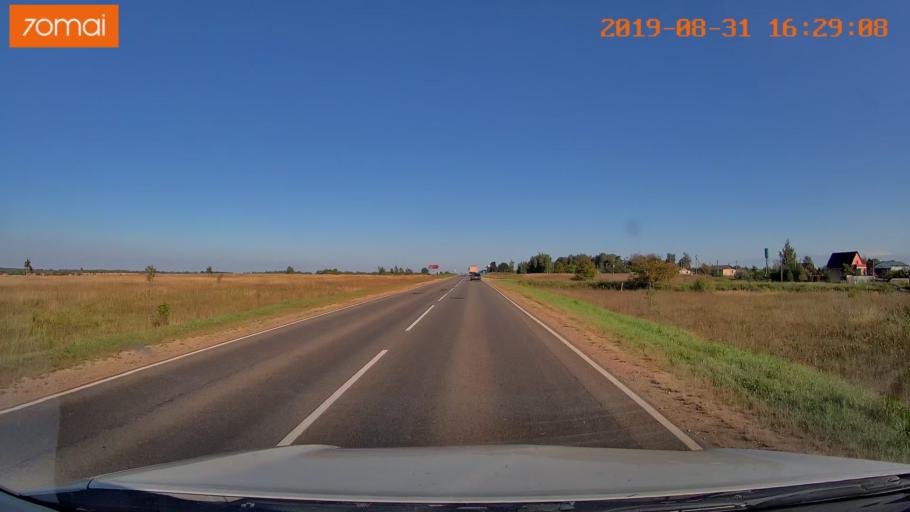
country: RU
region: Kaluga
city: Babynino
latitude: 54.5075
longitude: 35.7980
